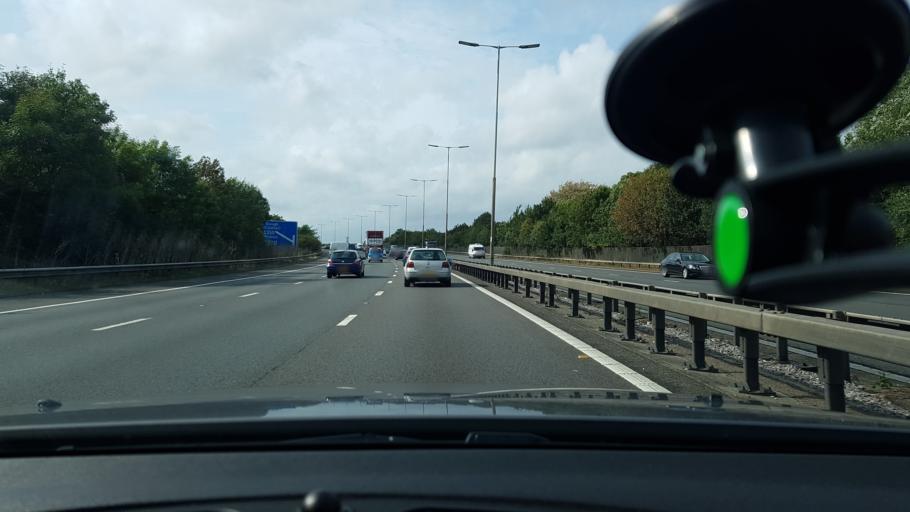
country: GB
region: England
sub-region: Slough
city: Slough
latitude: 51.5016
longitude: -0.5949
